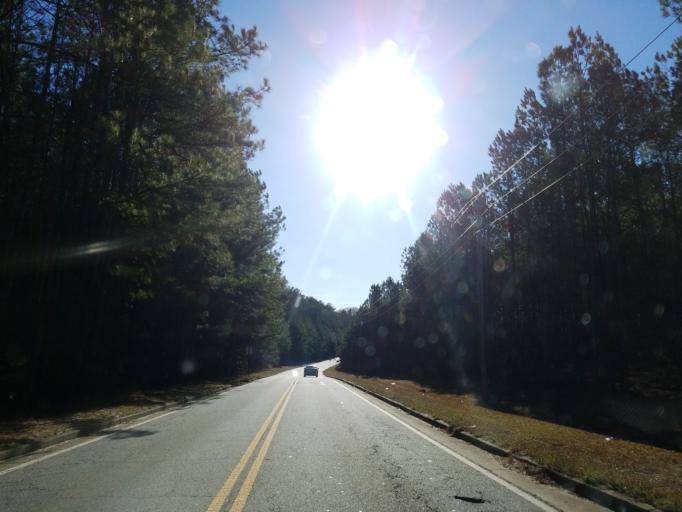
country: US
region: Georgia
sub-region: Cobb County
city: Mableton
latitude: 33.7940
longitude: -84.5179
